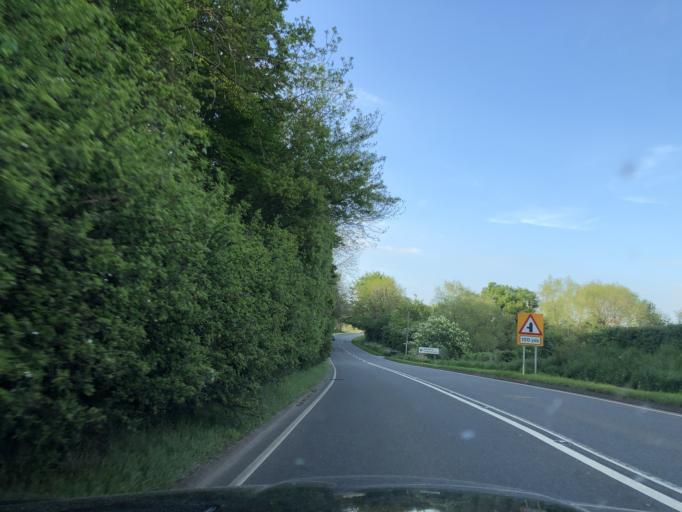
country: GB
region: England
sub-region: Warwickshire
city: Wellesbourne Mountford
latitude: 52.1281
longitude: -1.6160
